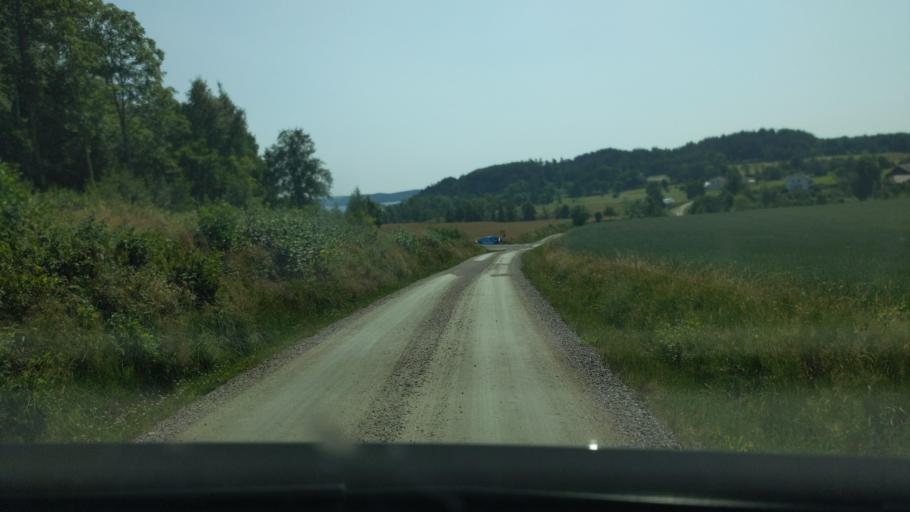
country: SE
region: Vaestra Goetaland
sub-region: Uddevalla Kommun
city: Uddevalla
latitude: 58.3391
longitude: 11.8102
